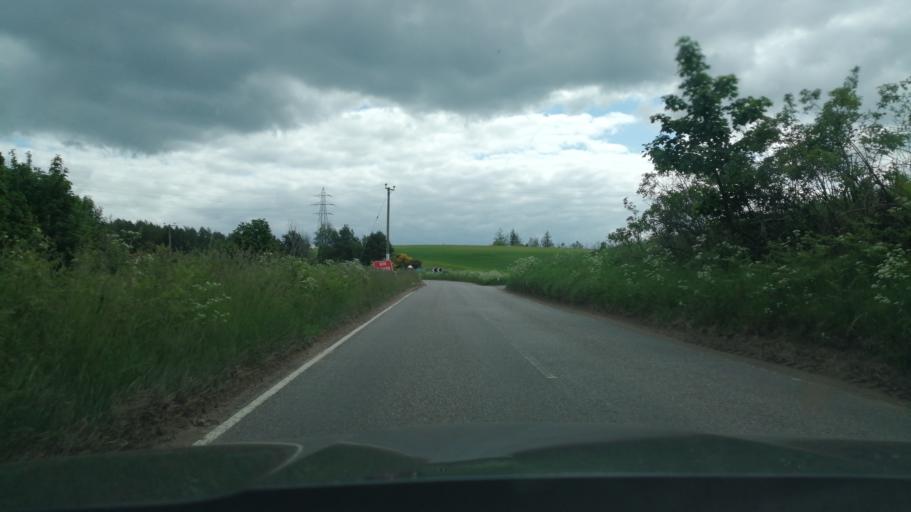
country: GB
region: Scotland
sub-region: Moray
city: Lhanbryd
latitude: 57.6205
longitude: -3.2169
